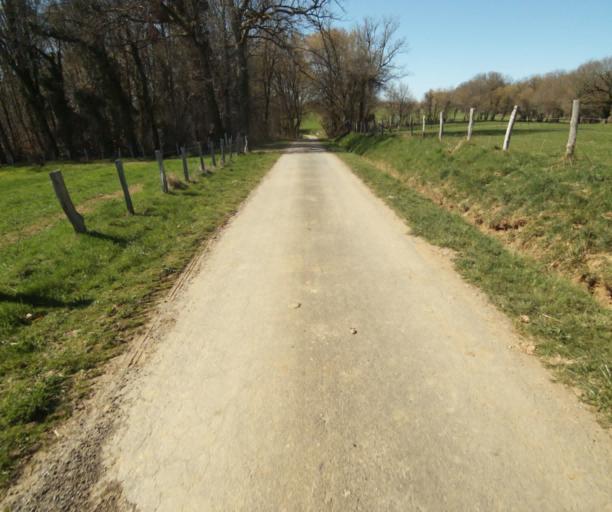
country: FR
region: Limousin
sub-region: Departement de la Correze
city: Chamboulive
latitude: 45.4140
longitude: 1.6392
